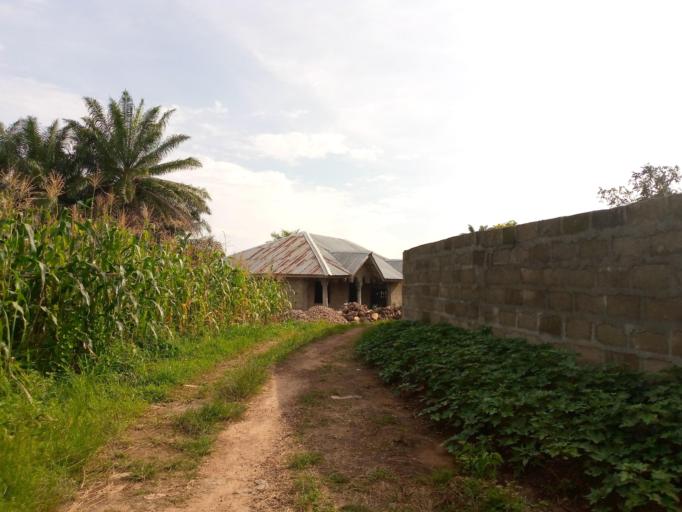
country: SL
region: Northern Province
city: Magburaka
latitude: 8.7179
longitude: -11.9542
